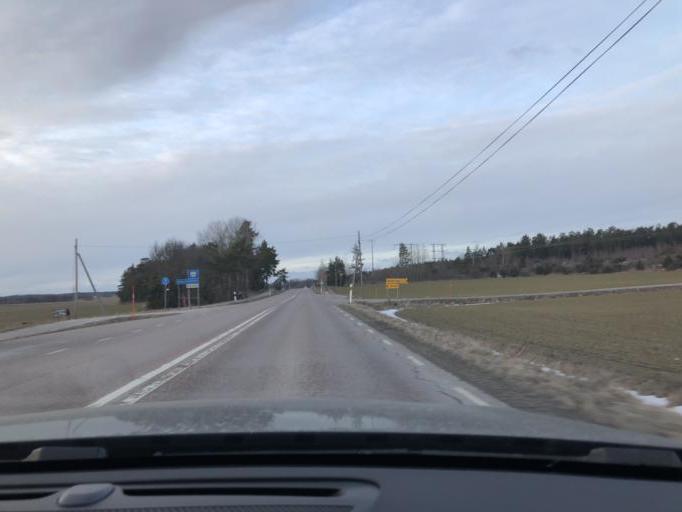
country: SE
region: Uppsala
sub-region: Uppsala Kommun
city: Gamla Uppsala
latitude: 59.9198
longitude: 17.6422
